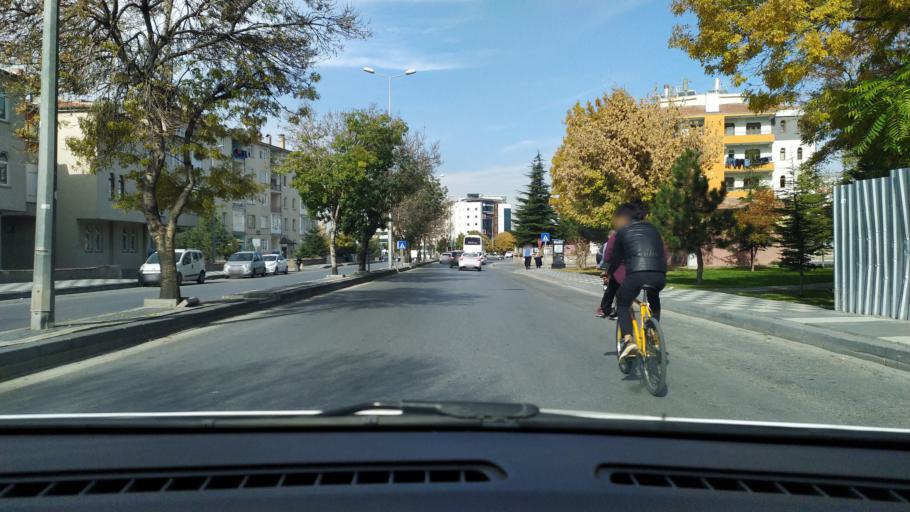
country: TR
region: Kayseri
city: Kayseri
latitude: 38.7097
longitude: 35.4914
